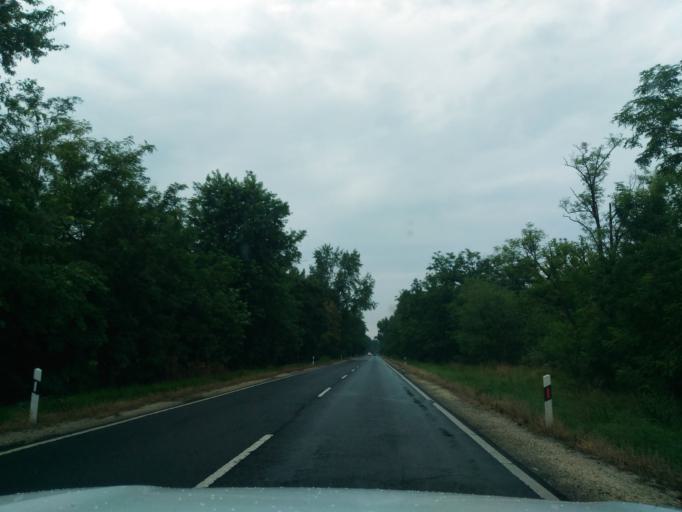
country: HU
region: Pest
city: Ocsa
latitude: 47.2716
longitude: 19.2078
